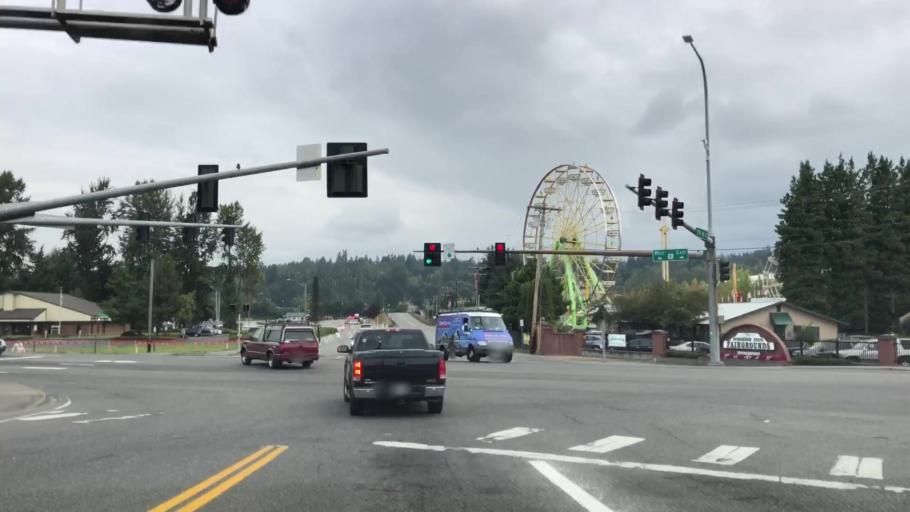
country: US
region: Washington
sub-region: Snohomish County
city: Monroe
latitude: 47.8654
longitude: -121.9908
